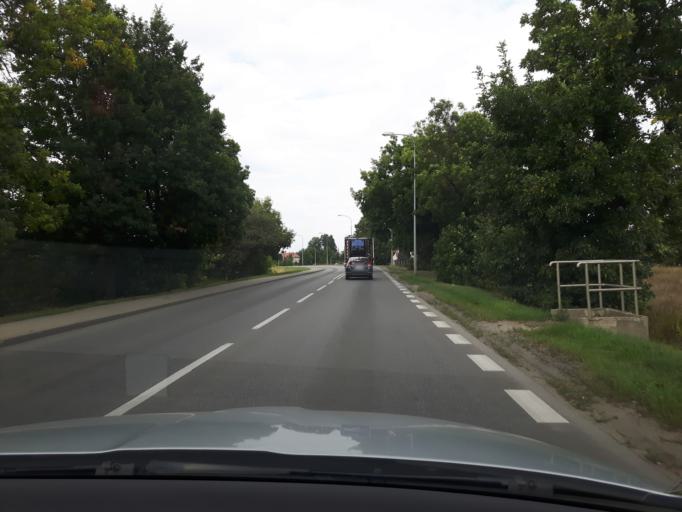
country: PL
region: Masovian Voivodeship
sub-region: Powiat legionowski
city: Stanislawow Pierwszy
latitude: 52.3509
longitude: 21.0294
